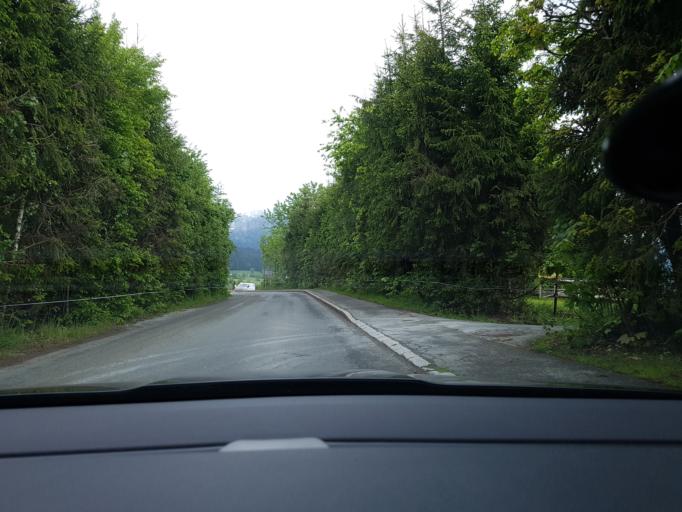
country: AT
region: Tyrol
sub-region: Politischer Bezirk Kitzbuhel
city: Oberndorf in Tirol
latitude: 47.5165
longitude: 12.3435
